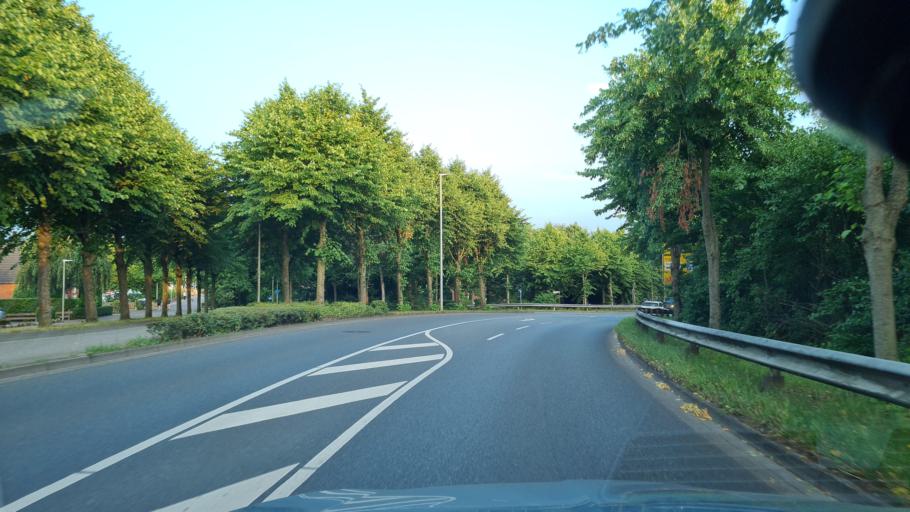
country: DE
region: Schleswig-Holstein
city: Husum
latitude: 54.4868
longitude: 9.0425
